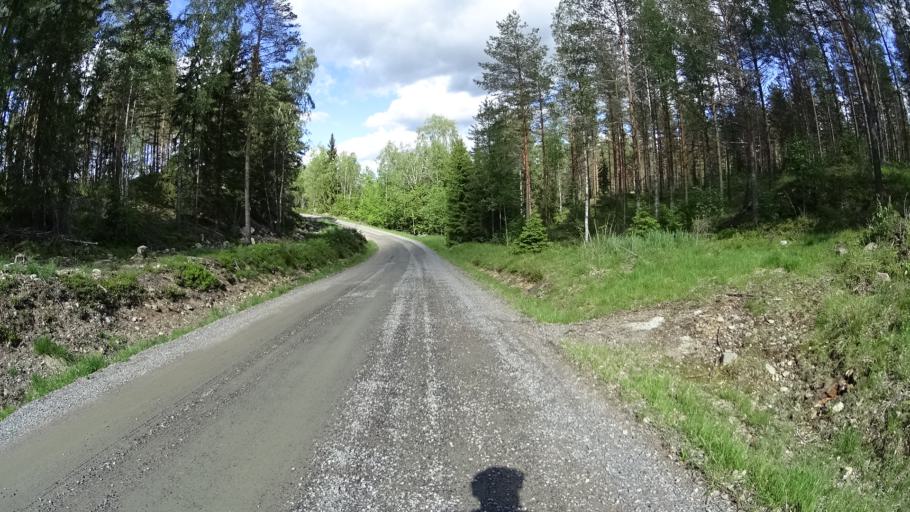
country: FI
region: Uusimaa
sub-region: Raaseporin
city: Pohja
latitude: 60.1759
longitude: 23.5867
